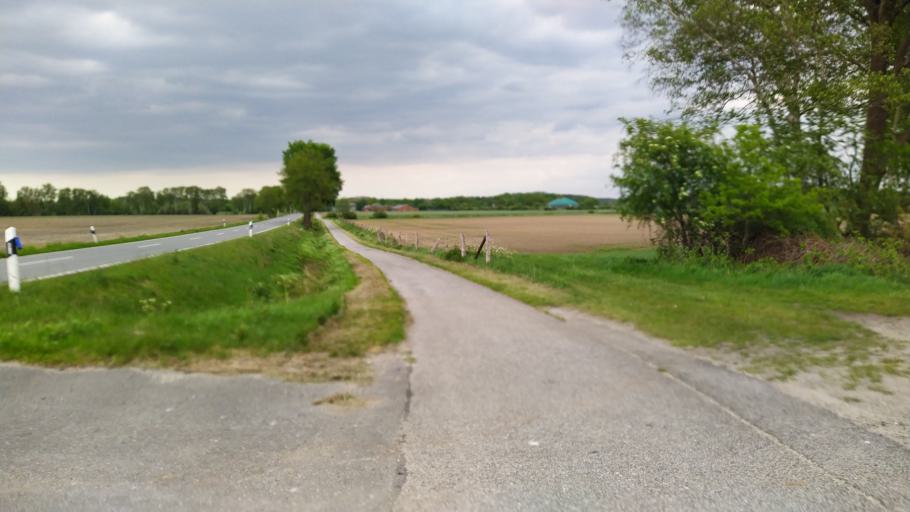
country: DE
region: Lower Saxony
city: Ostereistedt
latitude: 53.2644
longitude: 9.1907
